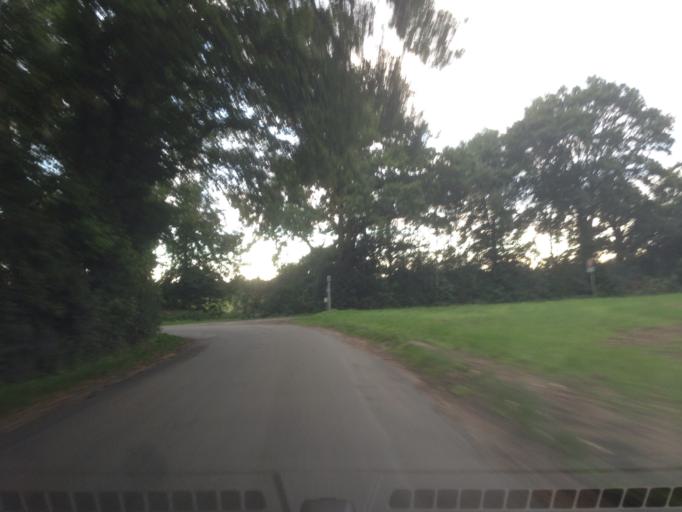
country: DE
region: North Rhine-Westphalia
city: Olfen
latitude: 51.7227
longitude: 7.3749
